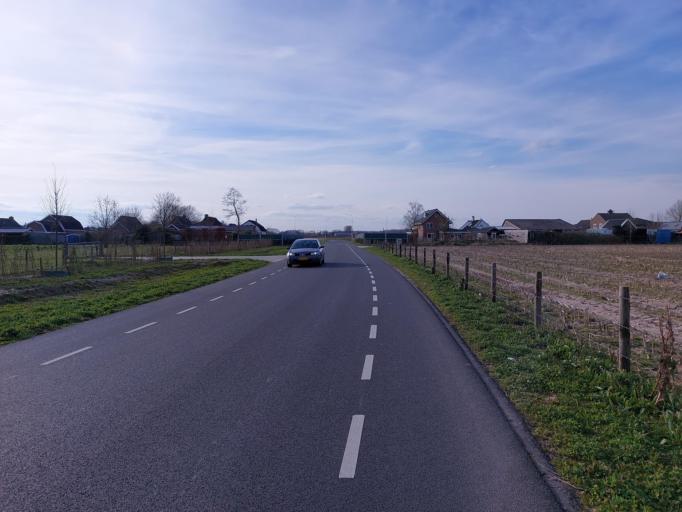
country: NL
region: Gelderland
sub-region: Gemeente Geldermalsen
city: Geldermalsen
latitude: 51.8932
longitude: 5.2754
